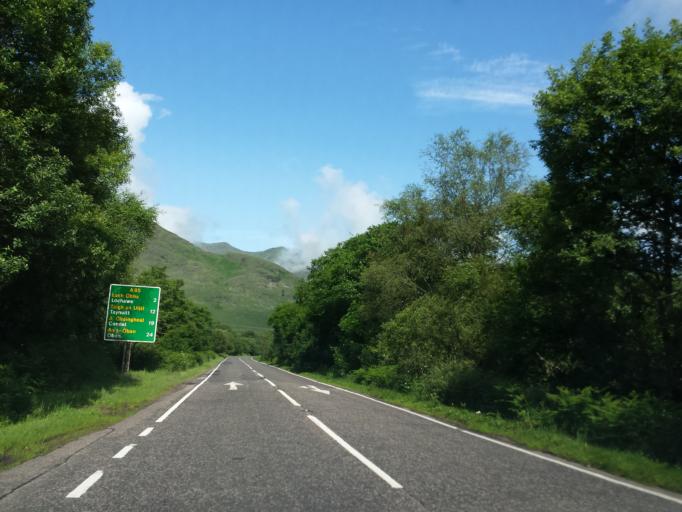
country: GB
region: Scotland
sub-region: Argyll and Bute
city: Garelochhead
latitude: 56.4057
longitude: -5.0128
